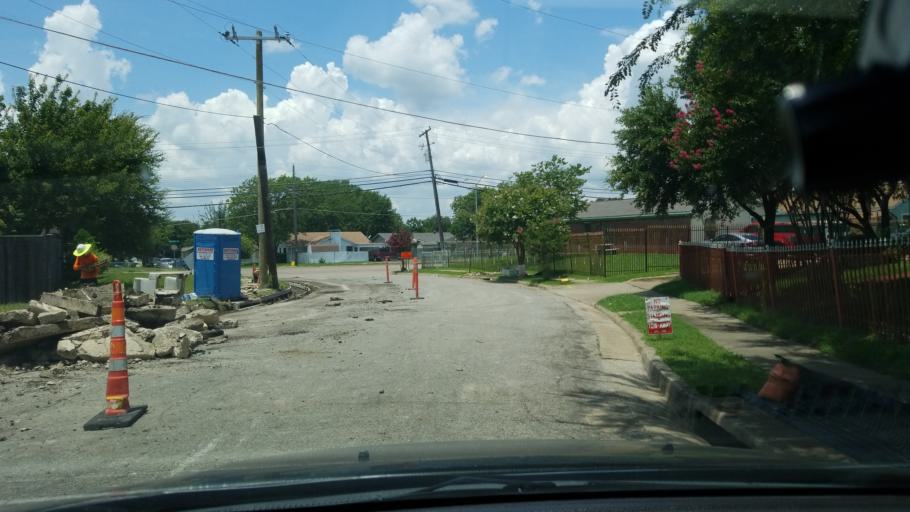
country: US
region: Texas
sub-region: Dallas County
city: Balch Springs
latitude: 32.7436
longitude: -96.6476
